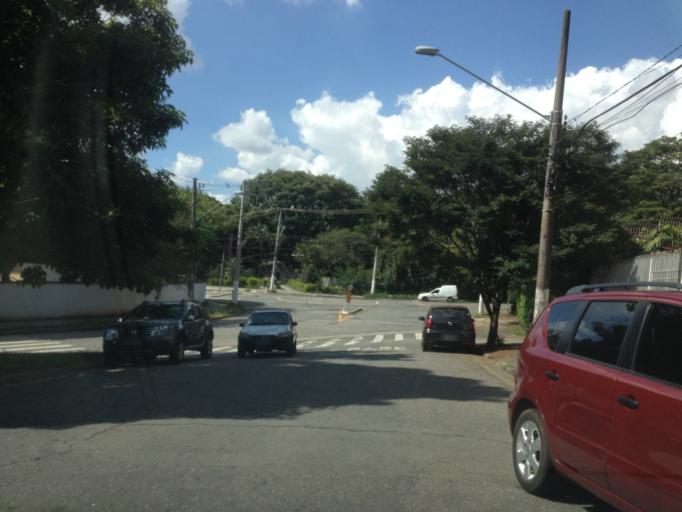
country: BR
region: Sao Paulo
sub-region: Osasco
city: Osasco
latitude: -23.5276
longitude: -46.7208
